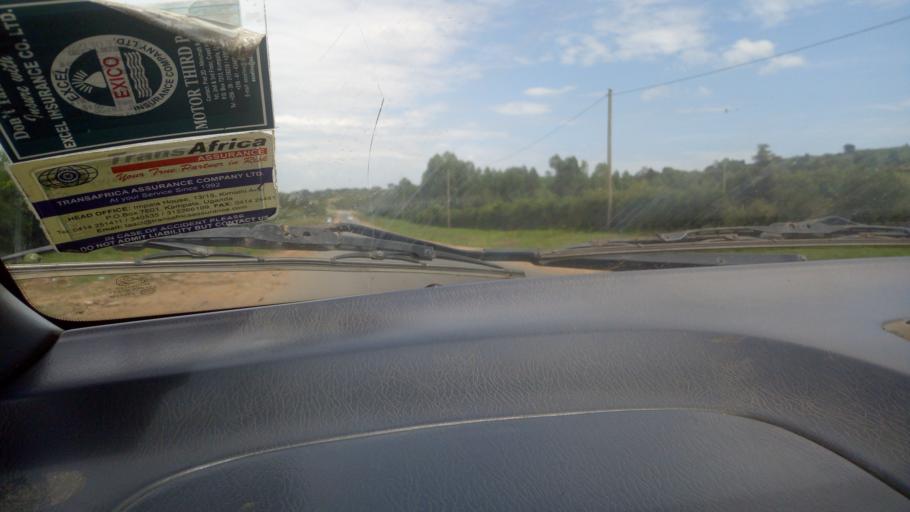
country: UG
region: Western Region
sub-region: Mbarara District
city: Bwizibwera
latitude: -0.4057
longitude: 30.5684
